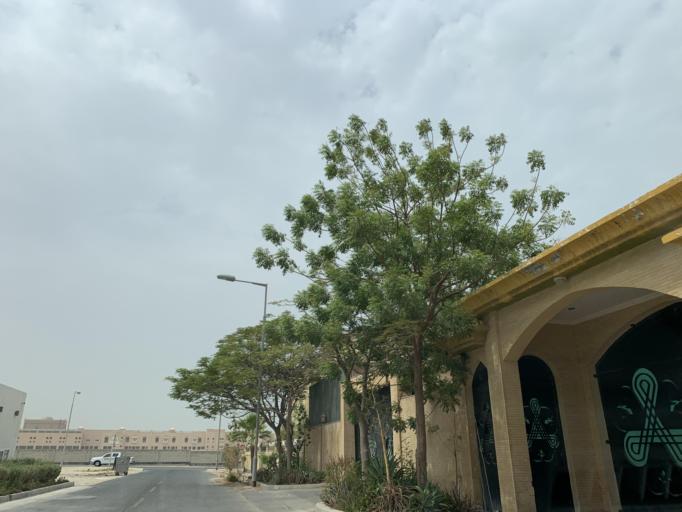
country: BH
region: Central Governorate
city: Madinat Hamad
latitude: 26.1791
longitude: 50.4776
